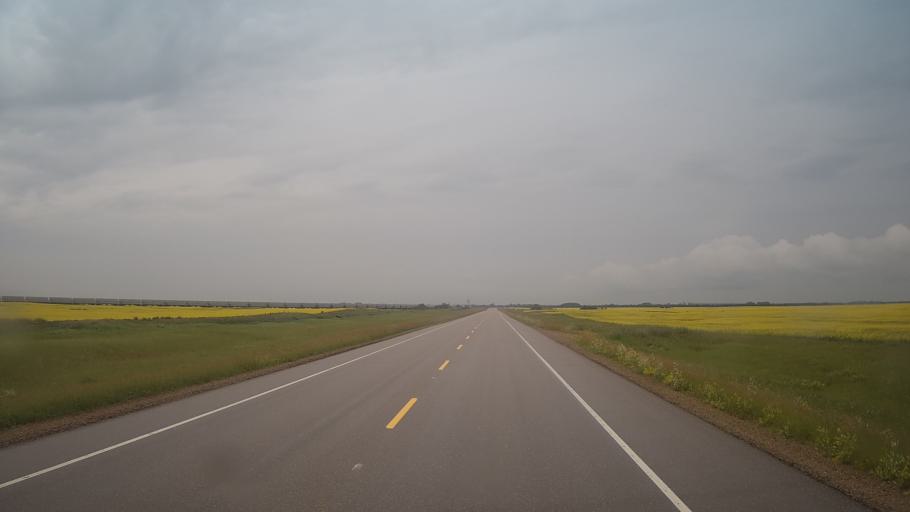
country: CA
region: Saskatchewan
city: Wilkie
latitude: 52.3006
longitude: -108.6736
